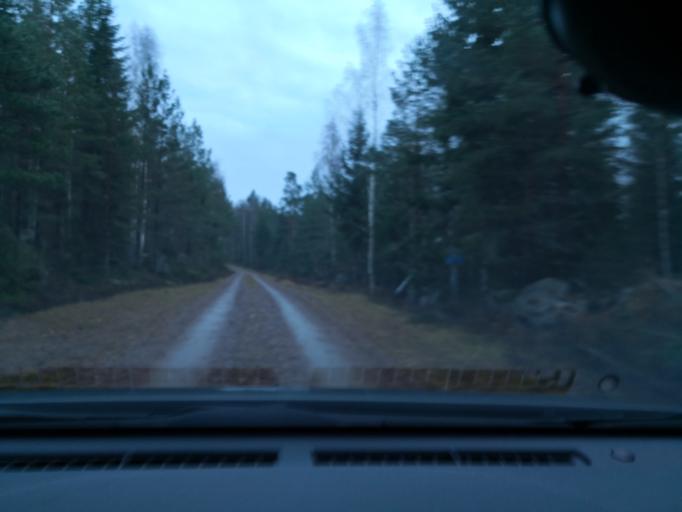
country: SE
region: Vaestmanland
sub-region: Hallstahammars Kommun
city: Kolback
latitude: 59.5506
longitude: 16.1676
